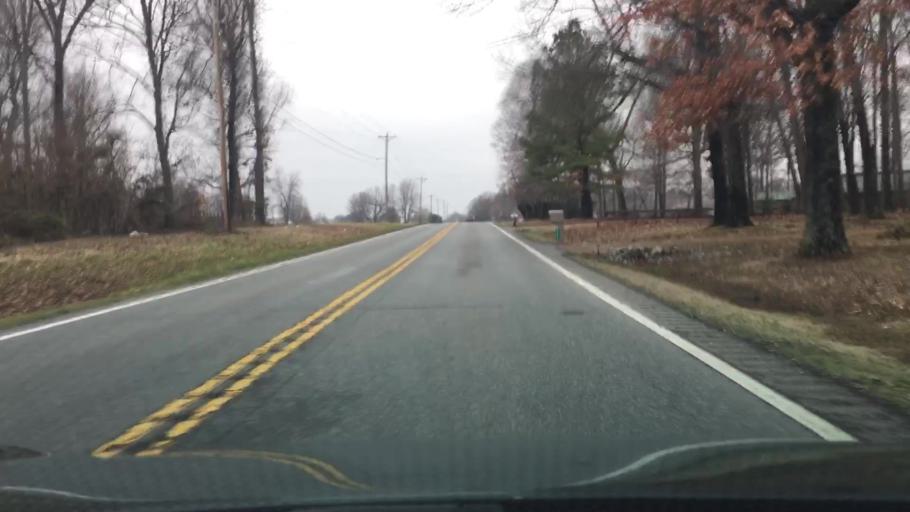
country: US
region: Kentucky
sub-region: Marshall County
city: Calvert City
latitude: 36.9514
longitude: -88.3691
